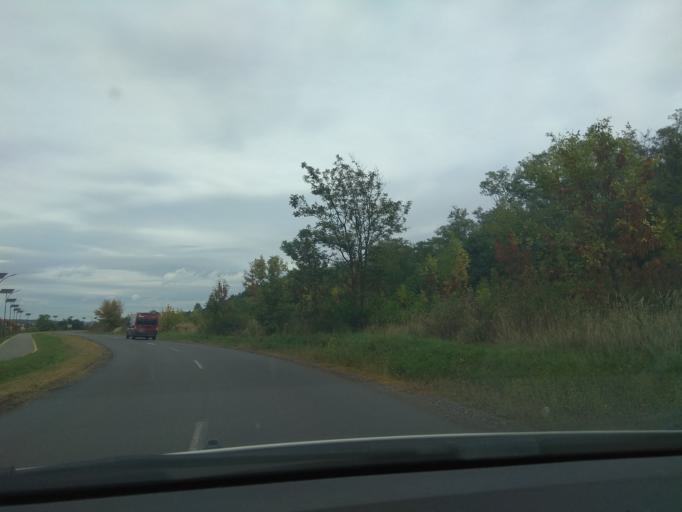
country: HU
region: Heves
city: Egerszalok
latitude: 47.8593
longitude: 20.3293
